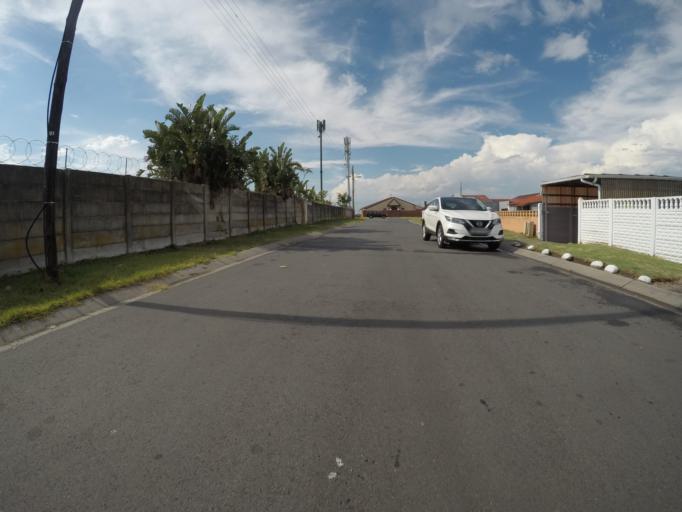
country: ZA
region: Eastern Cape
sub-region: Buffalo City Metropolitan Municipality
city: East London
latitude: -33.0228
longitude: 27.8725
